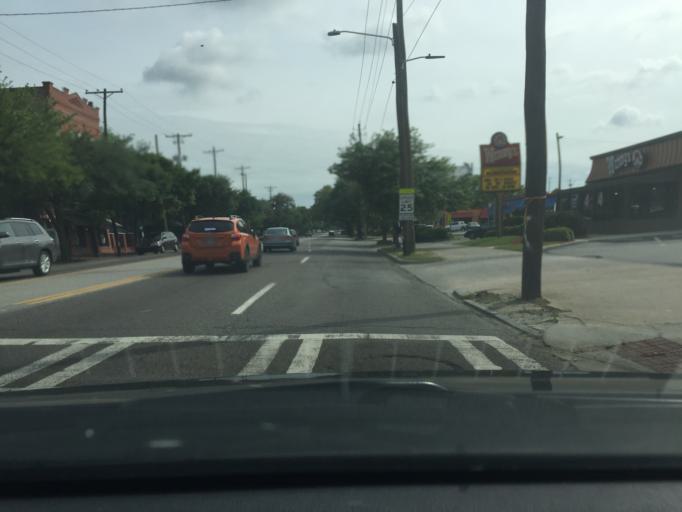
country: US
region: Georgia
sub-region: Chatham County
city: Savannah
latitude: 32.0717
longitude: -81.1006
